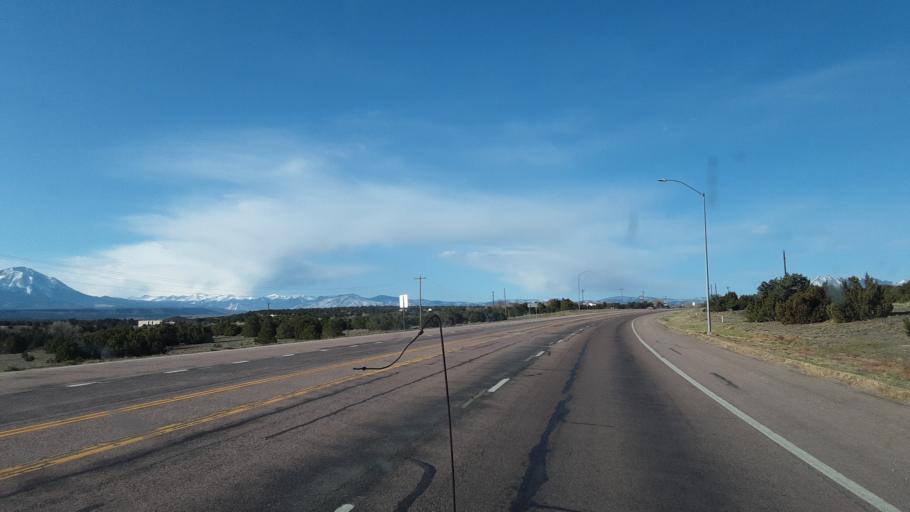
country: US
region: Colorado
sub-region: Huerfano County
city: Walsenburg
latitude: 37.6001
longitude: -104.8364
